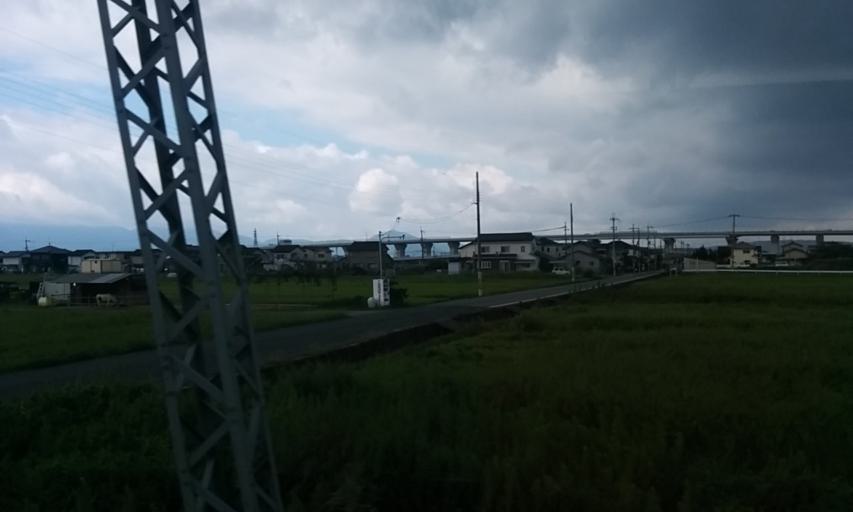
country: JP
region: Nara
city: Tawaramoto
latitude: 34.5673
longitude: 135.7864
